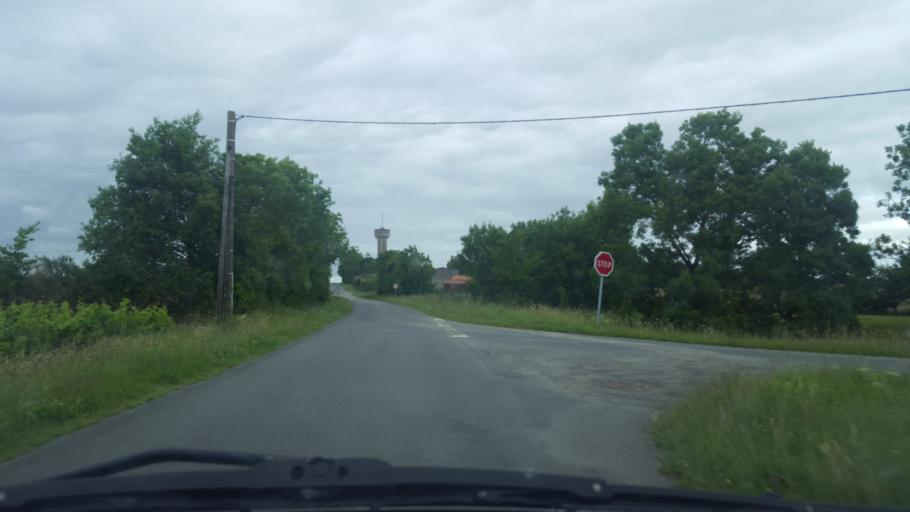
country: FR
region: Pays de la Loire
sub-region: Departement de la Loire-Atlantique
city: Saint-Philbert-de-Grand-Lieu
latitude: 47.0132
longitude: -1.6725
